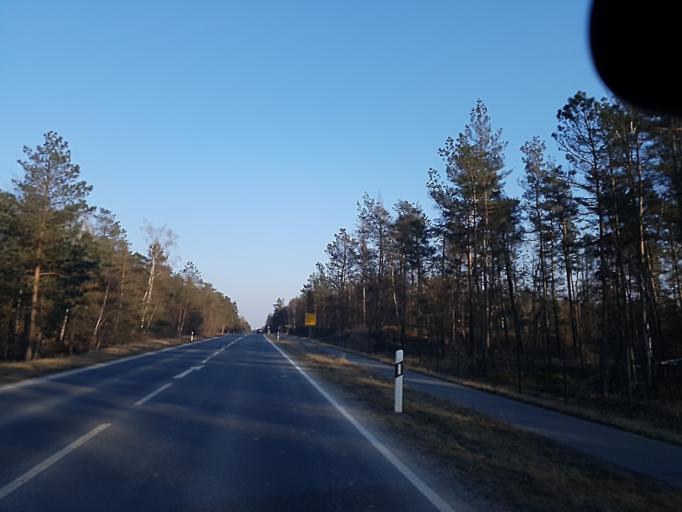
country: DE
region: Brandenburg
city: Sonnewalde
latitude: 51.6342
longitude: 13.6460
